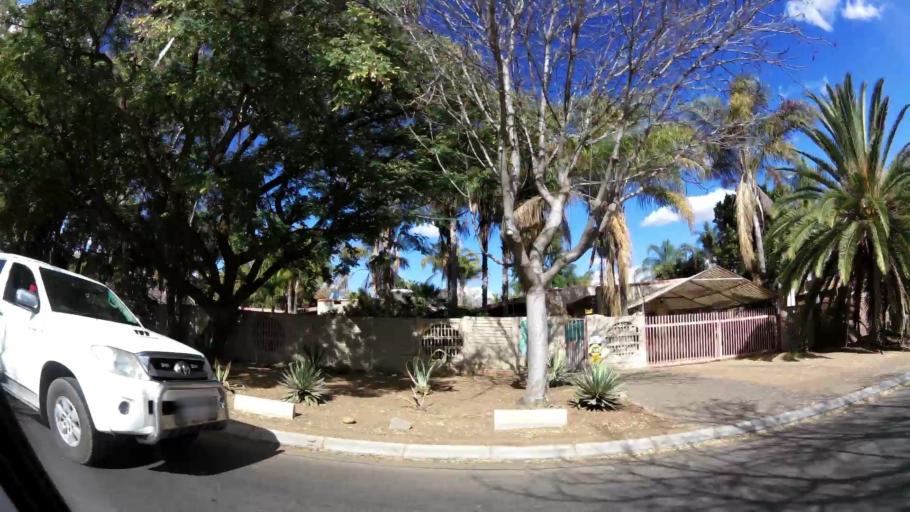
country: ZA
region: Limpopo
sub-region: Capricorn District Municipality
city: Polokwane
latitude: -23.8851
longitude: 29.4611
